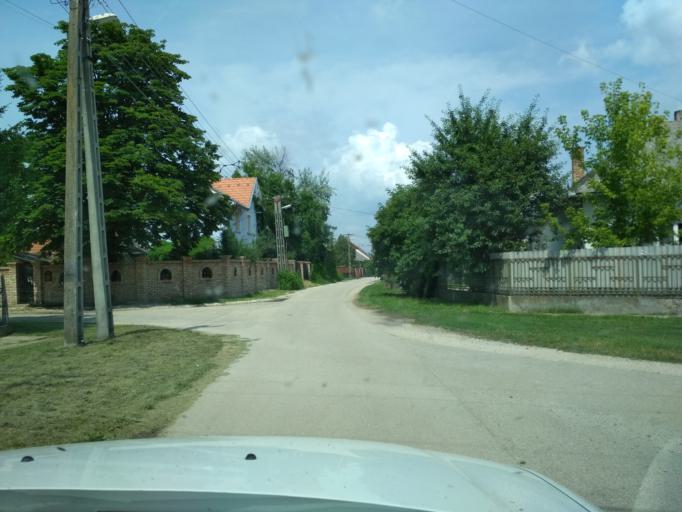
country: HU
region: Pest
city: Tapioszentmarton
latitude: 47.3375
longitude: 19.7477
